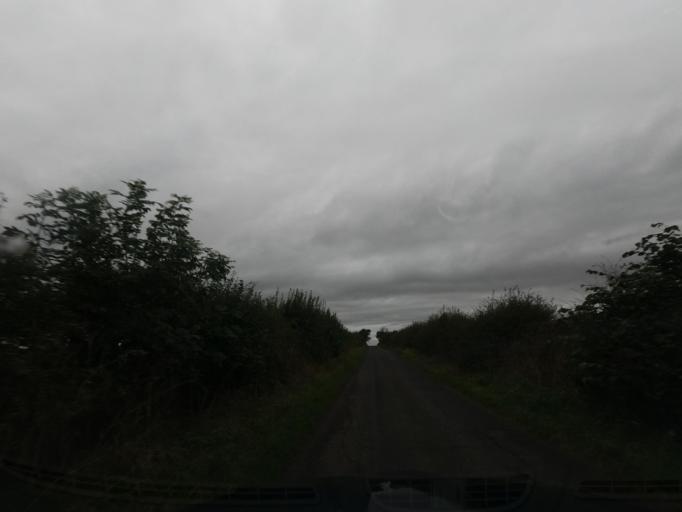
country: GB
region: England
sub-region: Northumberland
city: Ford
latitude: 55.7096
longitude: -2.0876
